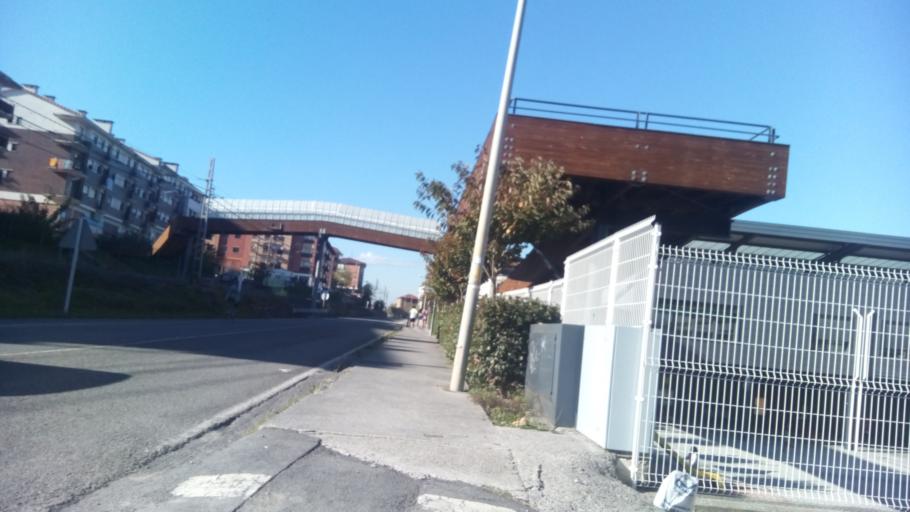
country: ES
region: Basque Country
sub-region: Bizkaia
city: Zamudio
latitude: 43.2828
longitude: -2.8600
